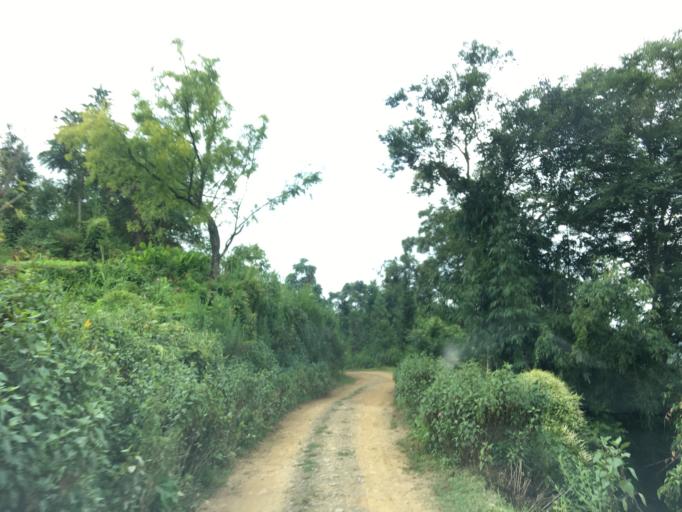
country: CN
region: Guangxi Zhuangzu Zizhiqu
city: Xinzhou
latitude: 24.8868
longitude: 105.8418
